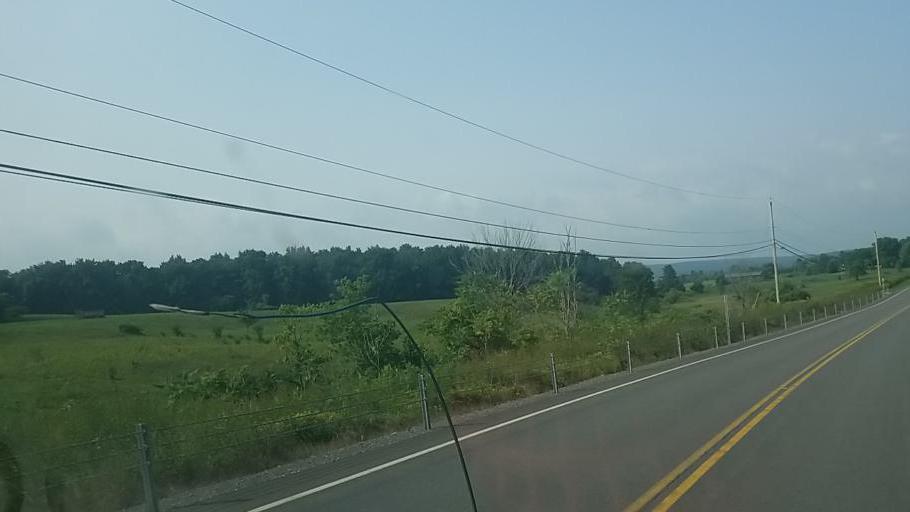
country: US
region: New York
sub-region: Fulton County
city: Johnstown
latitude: 42.9981
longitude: -74.4094
